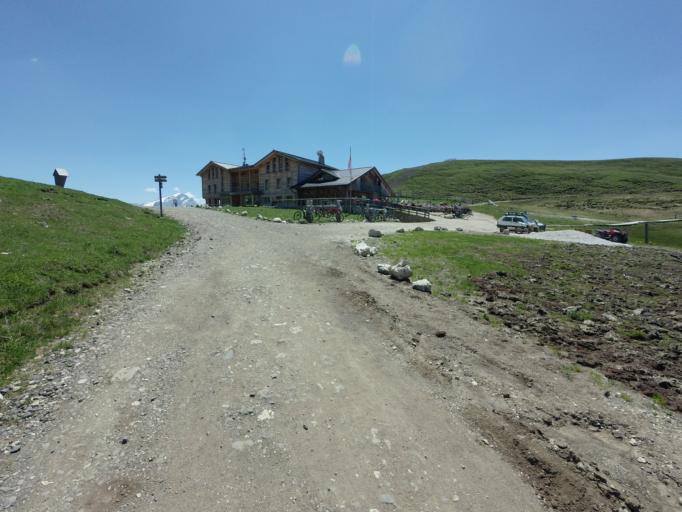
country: IT
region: Trentino-Alto Adige
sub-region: Provincia di Trento
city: Mazzin
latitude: 46.5048
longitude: 11.7005
